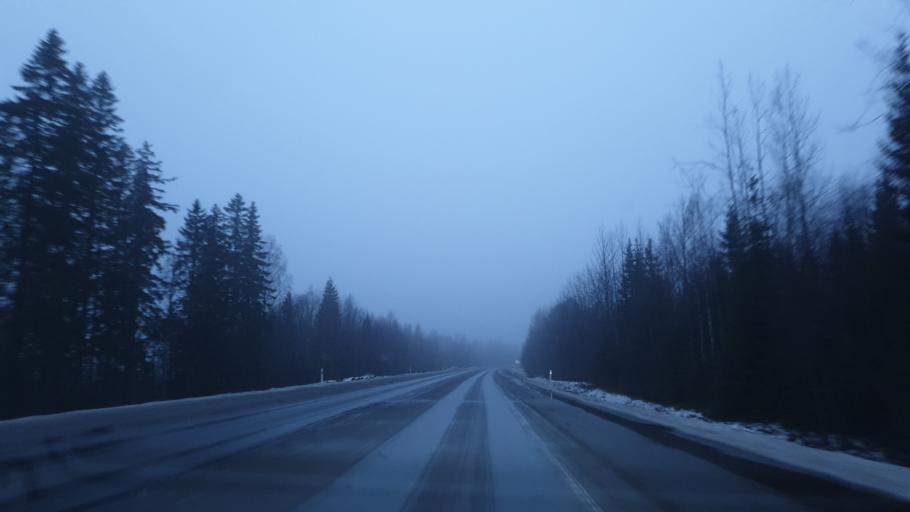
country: SE
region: Vaesterbotten
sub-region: Umea Kommun
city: Holmsund
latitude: 63.7529
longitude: 20.3633
